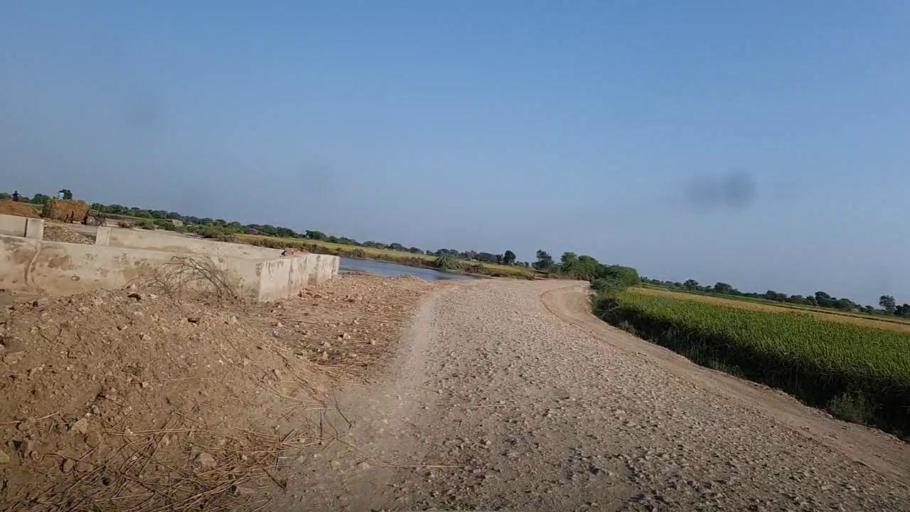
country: PK
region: Sindh
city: Bulri
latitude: 24.7515
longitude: 68.4194
